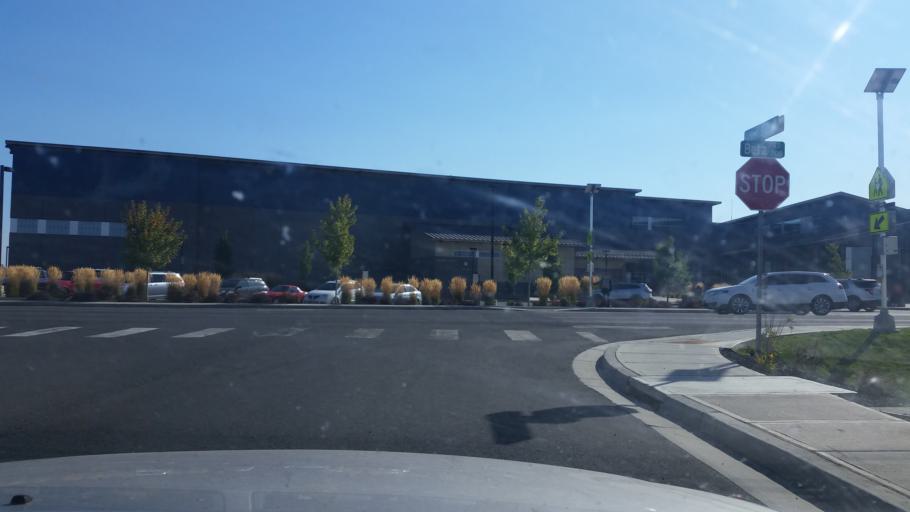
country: US
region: Washington
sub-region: Spokane County
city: Cheney
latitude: 47.5075
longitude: -117.5790
